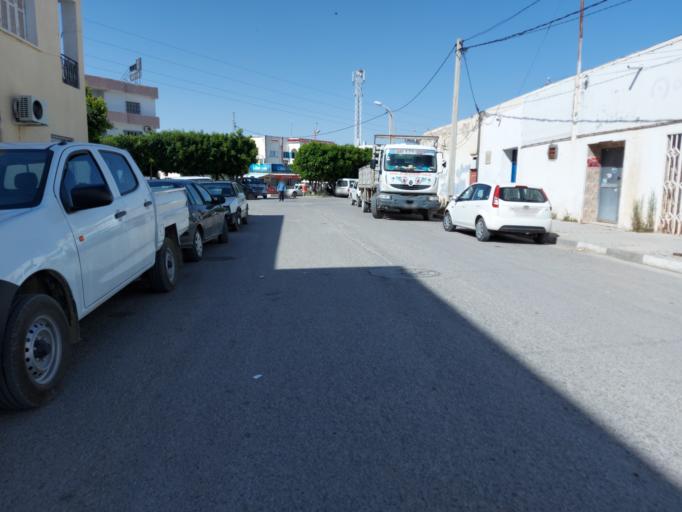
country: TN
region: Silyanah
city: Siliana
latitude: 36.0851
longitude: 9.3682
